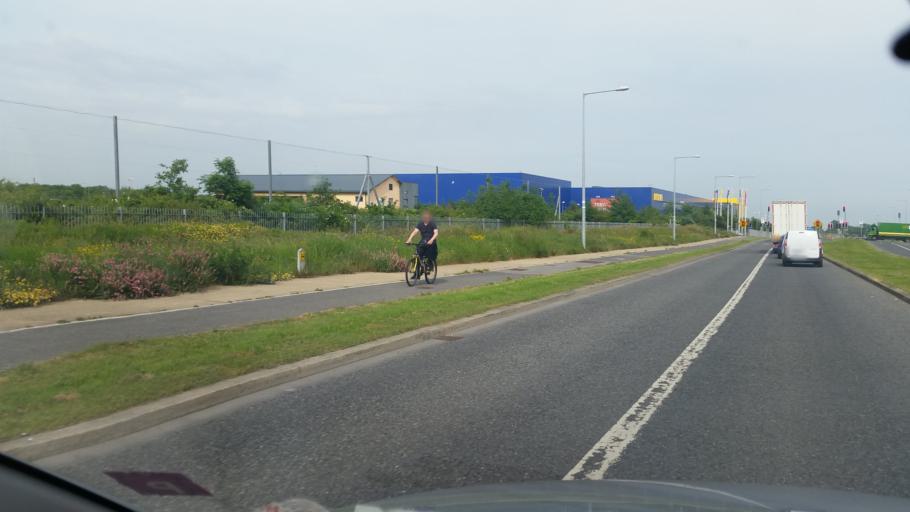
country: IE
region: Leinster
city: Ballymun
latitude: 53.4060
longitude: -6.2808
